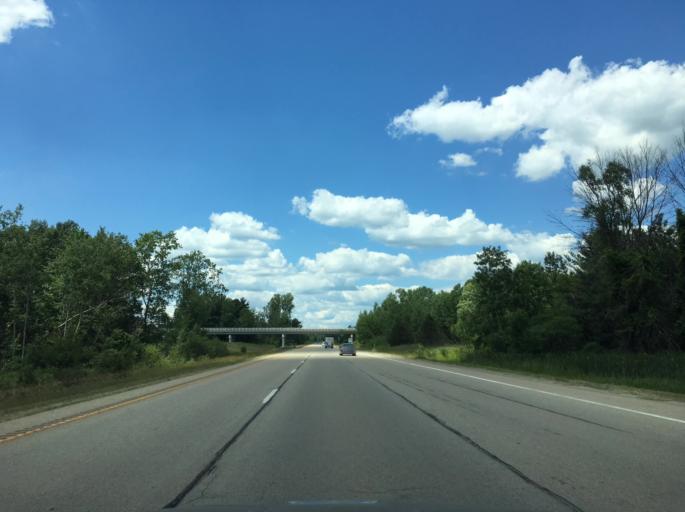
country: US
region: Michigan
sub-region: Clare County
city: Clare
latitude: 43.8809
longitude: -84.7851
